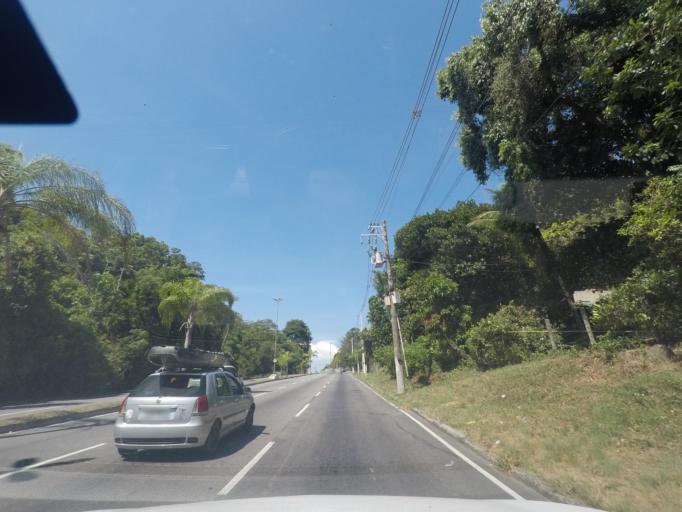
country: BR
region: Rio de Janeiro
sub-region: Niteroi
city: Niteroi
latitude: -22.9222
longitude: -43.0556
